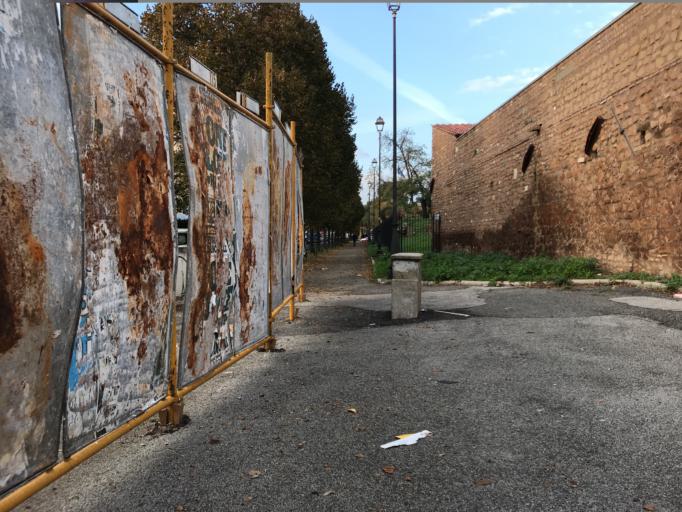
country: IT
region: Latium
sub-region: Citta metropolitana di Roma Capitale
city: Rome
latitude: 41.8996
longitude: 12.5089
